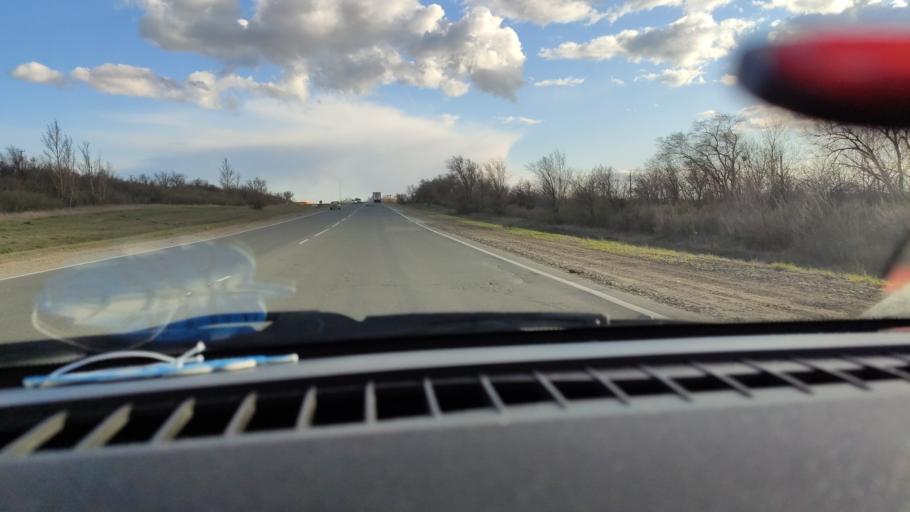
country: RU
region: Saratov
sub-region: Saratovskiy Rayon
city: Saratov
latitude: 51.6811
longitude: 46.0015
